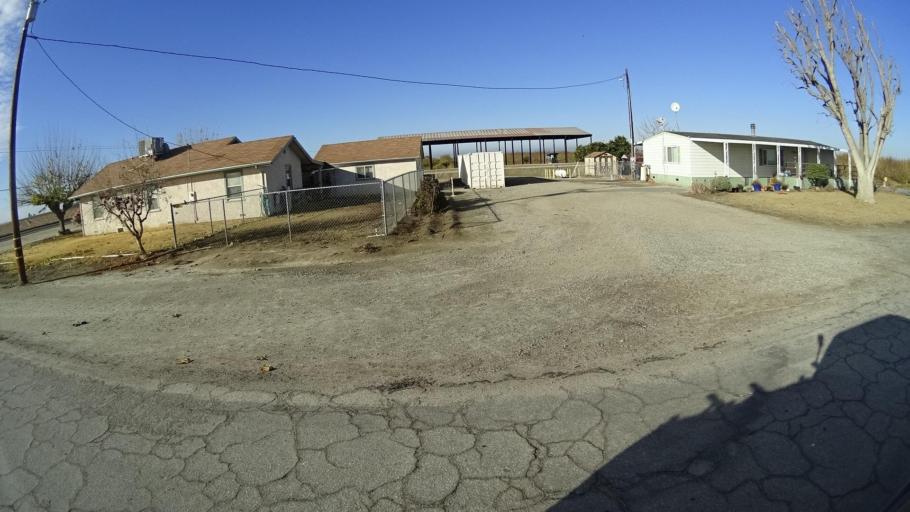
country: US
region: California
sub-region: Kern County
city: Delano
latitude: 35.7182
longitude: -119.3030
